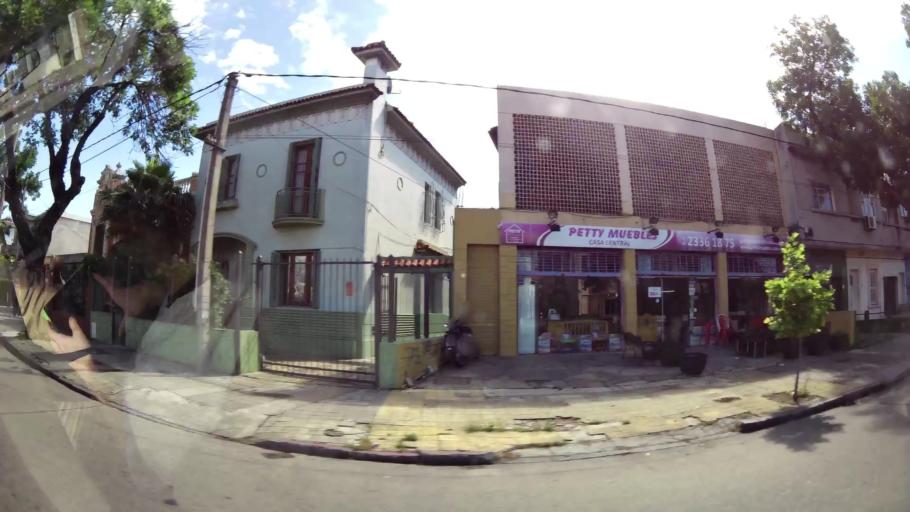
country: UY
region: Montevideo
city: Montevideo
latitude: -34.8624
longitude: -56.1934
